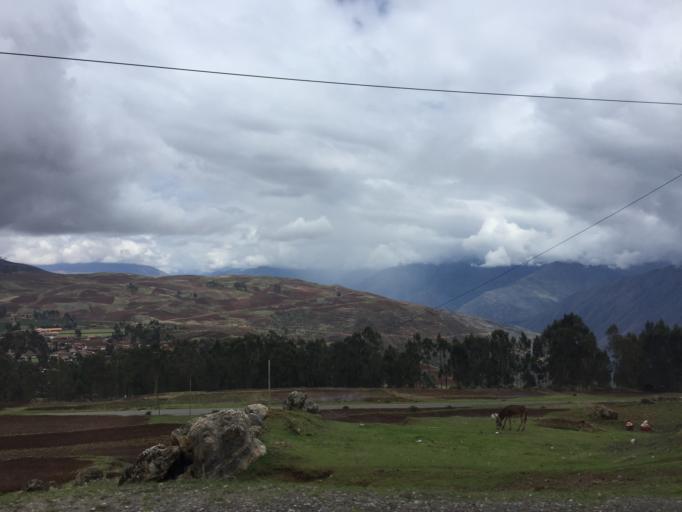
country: PE
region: Cusco
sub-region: Provincia de Urubamba
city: Huayllabamba
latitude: -13.3667
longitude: -72.0687
